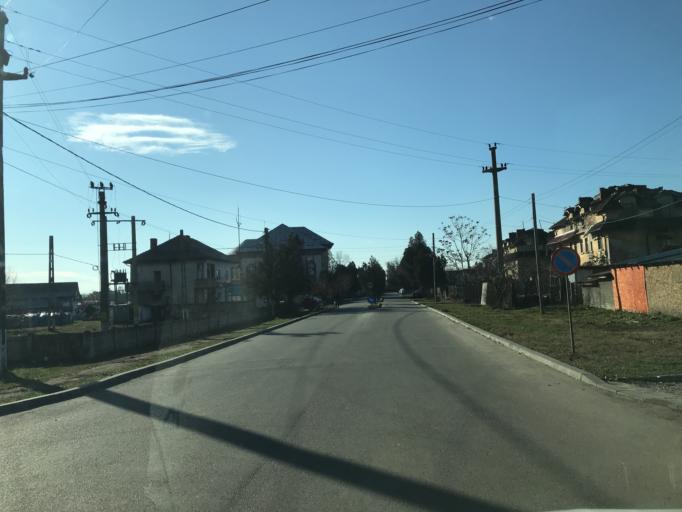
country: RO
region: Olt
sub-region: Comuna Piatra Olt
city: Piatra Olt
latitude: 44.3690
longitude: 24.2598
